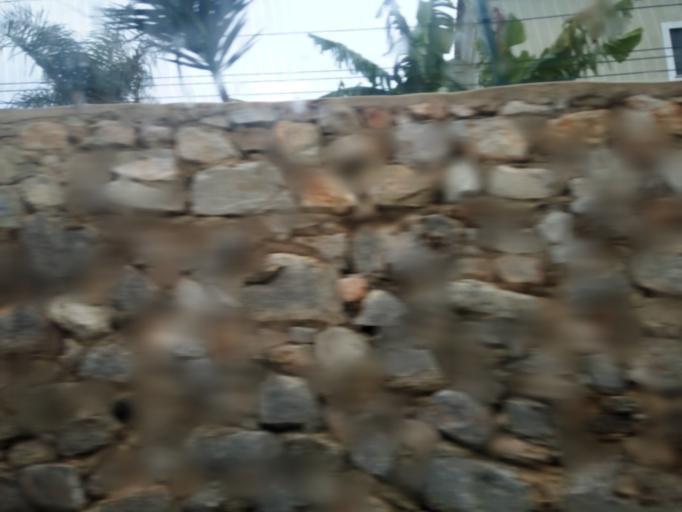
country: PT
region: Faro
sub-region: Faro
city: Santa Barbara de Nexe
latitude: 37.1060
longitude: -7.9764
